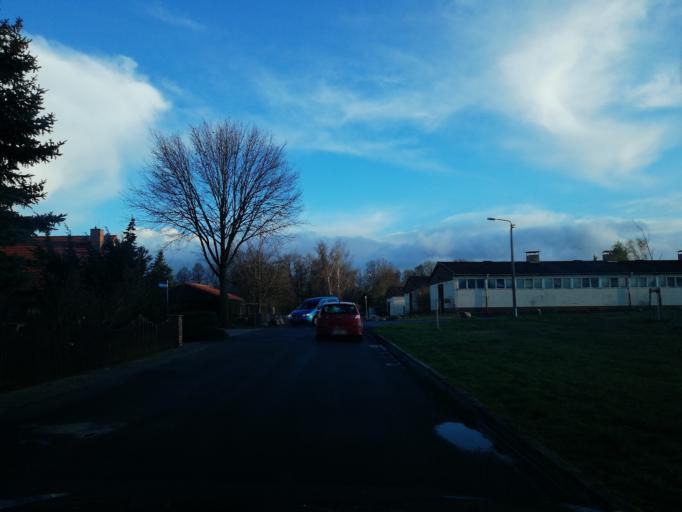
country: DE
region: Brandenburg
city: Calau
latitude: 51.7371
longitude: 13.9651
